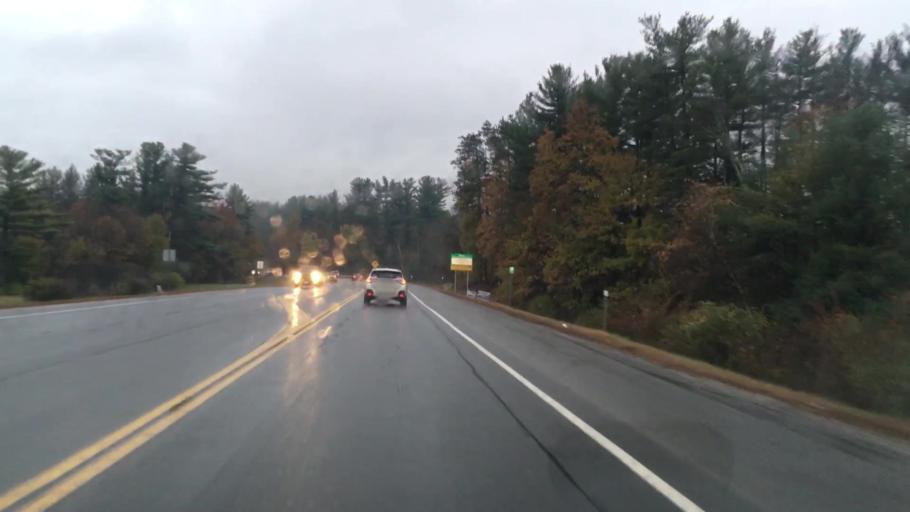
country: US
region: New Hampshire
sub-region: Hillsborough County
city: Wilton
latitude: 42.8391
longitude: -71.7025
